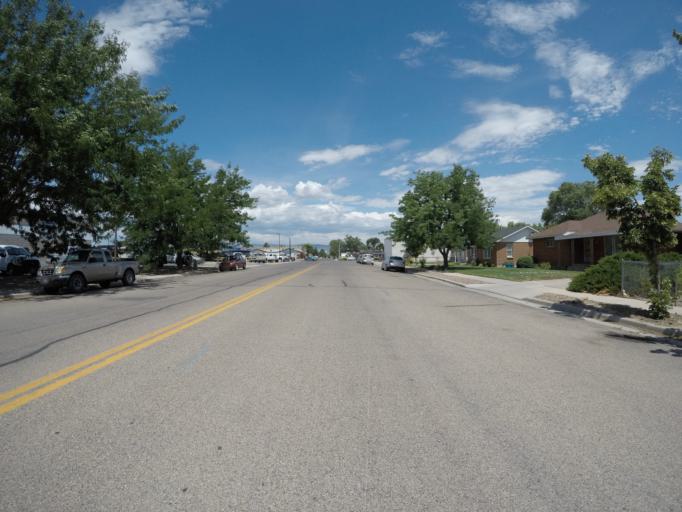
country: US
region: Utah
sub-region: Uintah County
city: Vernal
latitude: 40.4547
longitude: -109.5349
